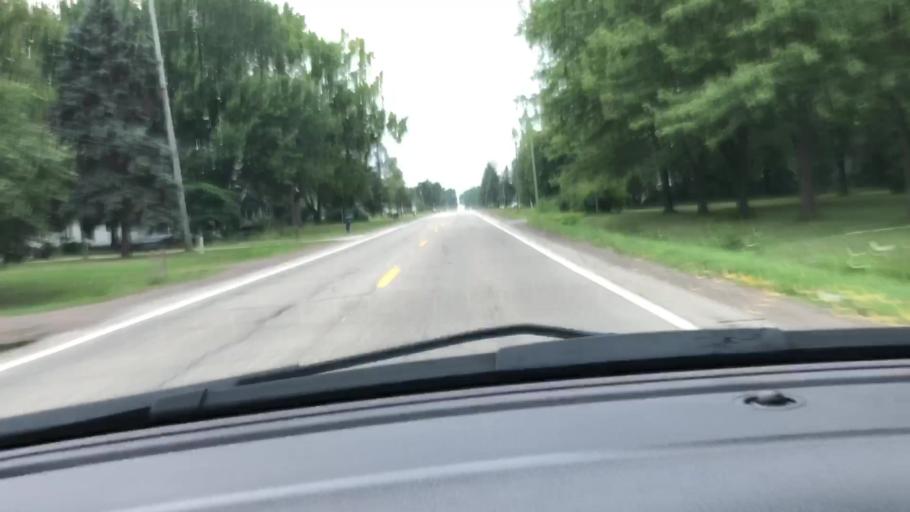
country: US
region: Michigan
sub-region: Bay County
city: Auburn
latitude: 43.6043
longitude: -84.1311
